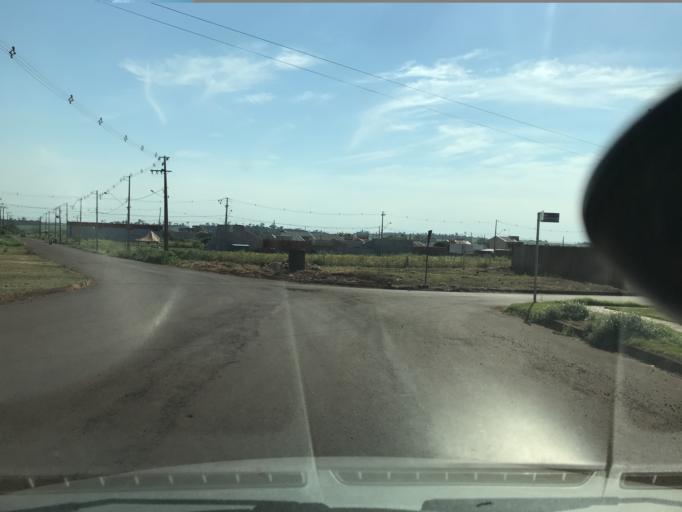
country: BR
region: Parana
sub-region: Palotina
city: Palotina
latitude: -24.2947
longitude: -53.8302
